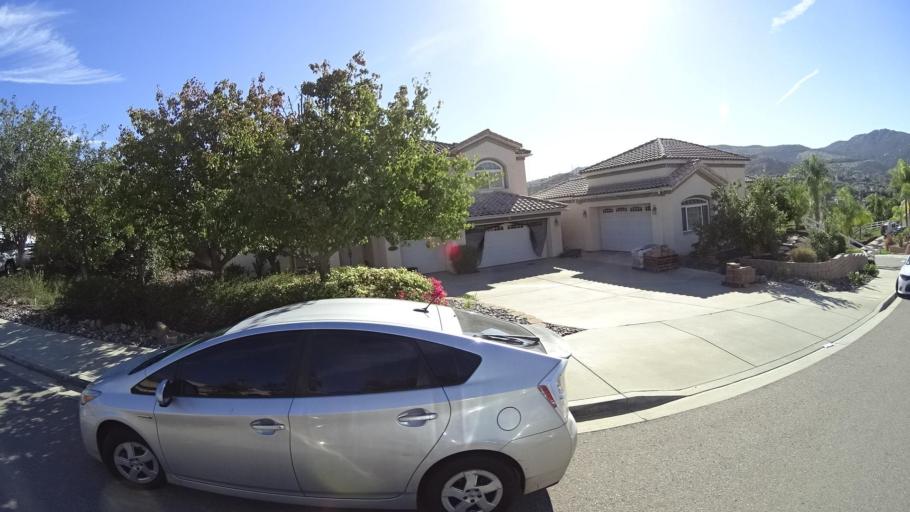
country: US
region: California
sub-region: San Diego County
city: Lakeside
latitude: 32.8444
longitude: -116.8922
